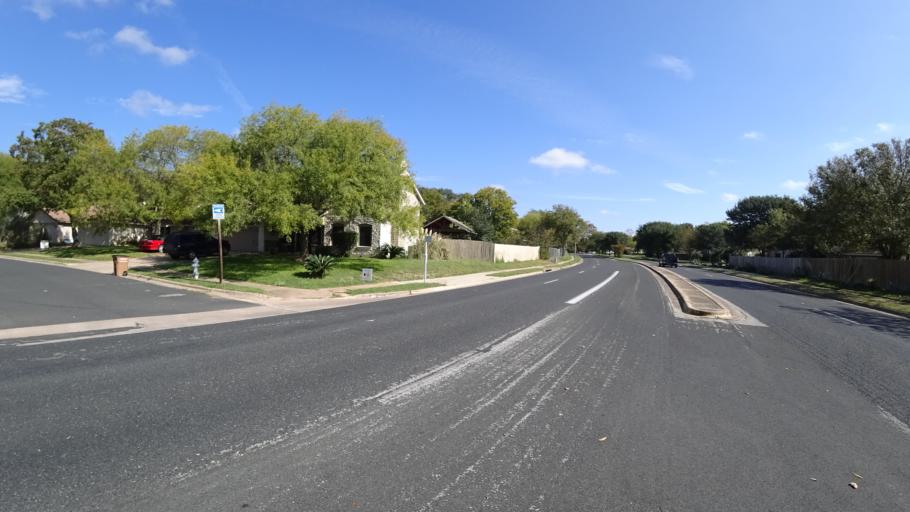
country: US
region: Texas
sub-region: Travis County
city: Shady Hollow
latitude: 30.1993
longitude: -97.8222
